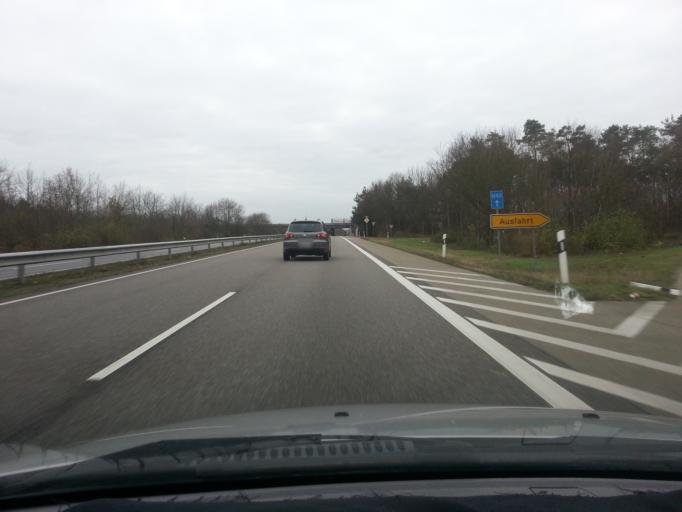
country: DE
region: Baden-Wuerttemberg
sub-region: Karlsruhe Region
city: Hockenheim
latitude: 49.3357
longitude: 8.5461
